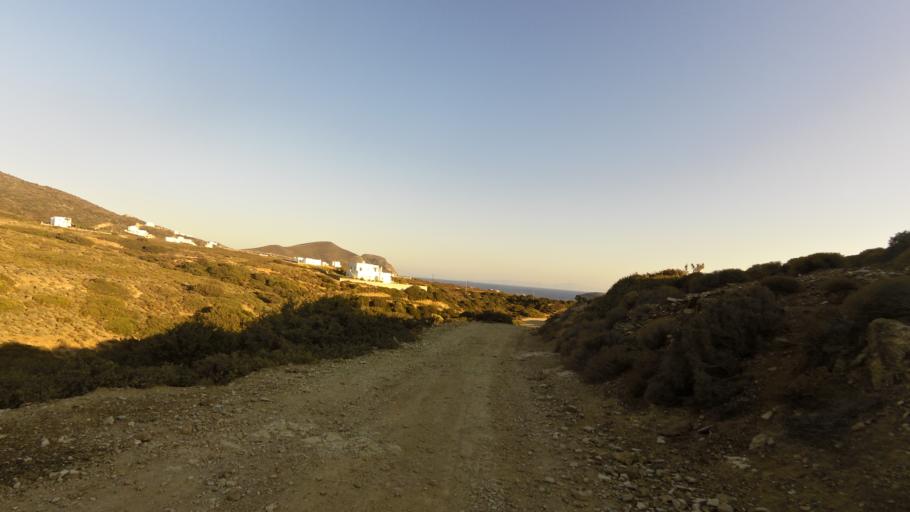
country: GR
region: South Aegean
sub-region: Nomos Kykladon
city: Antiparos
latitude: 36.9838
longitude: 25.0292
